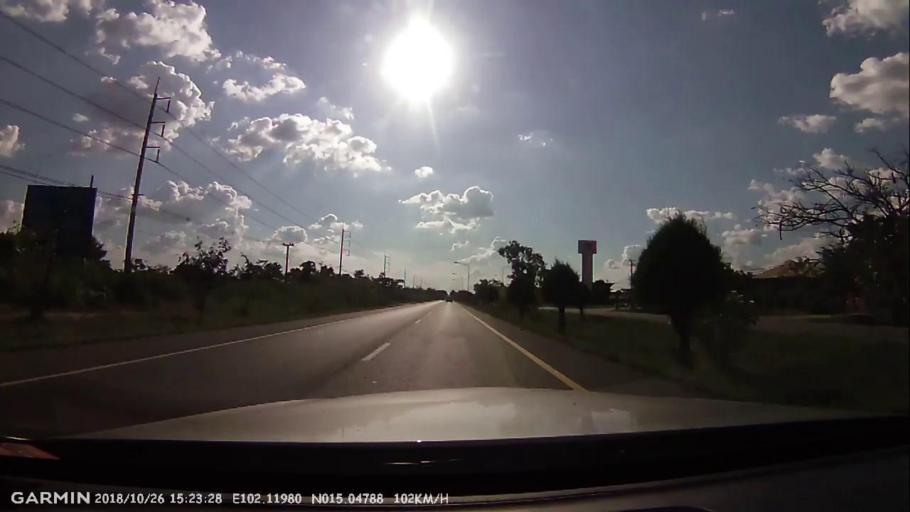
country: TH
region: Nakhon Ratchasima
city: Nakhon Ratchasima
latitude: 15.0479
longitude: 102.1198
